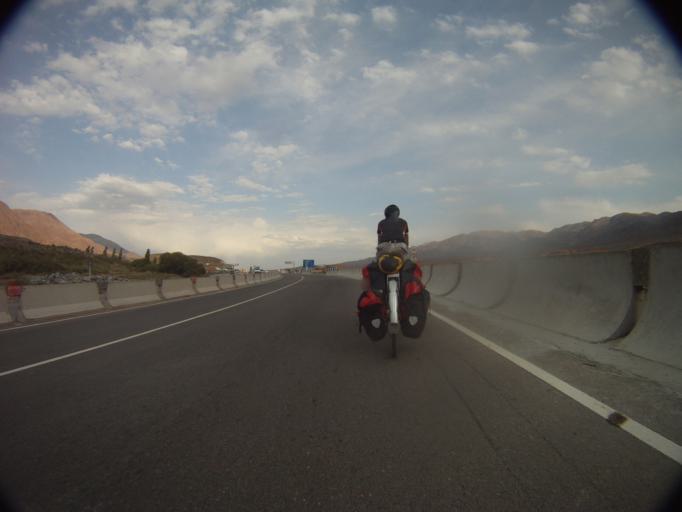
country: KG
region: Naryn
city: Kochkor
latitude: 42.4723
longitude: 75.8756
